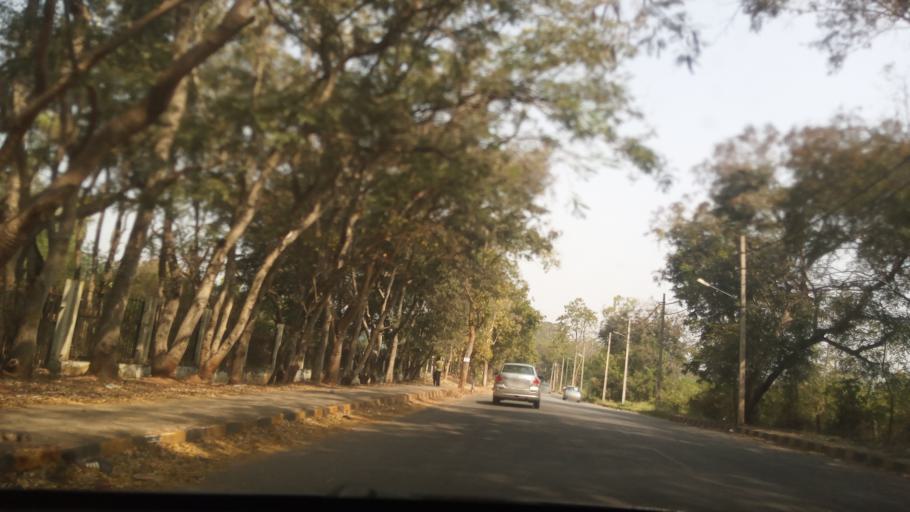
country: IN
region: Karnataka
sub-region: Mysore
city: Mysore
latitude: 12.3110
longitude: 76.6266
